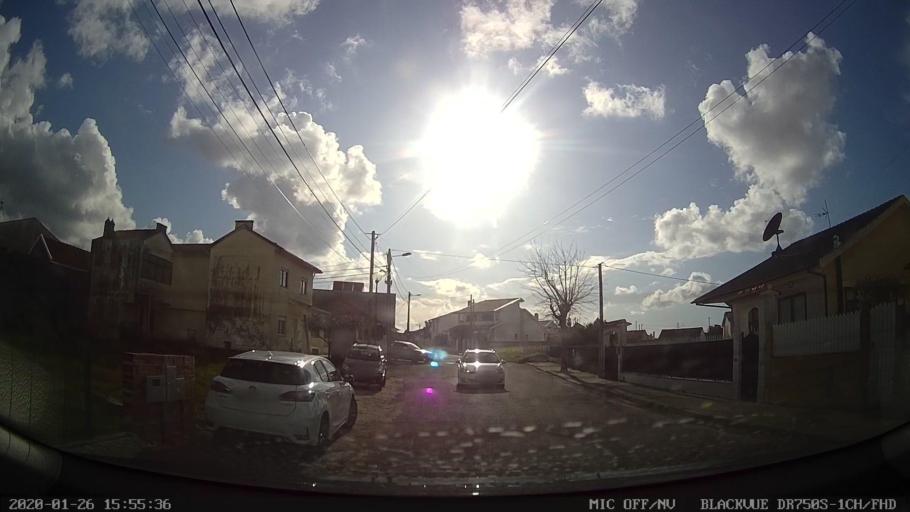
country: PT
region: Aveiro
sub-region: Aveiro
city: Aradas
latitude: 40.6291
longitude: -8.6284
